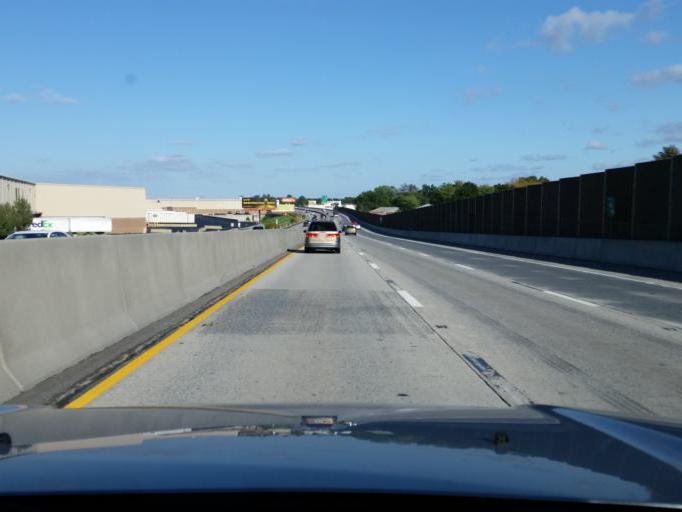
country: US
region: Pennsylvania
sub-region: Cumberland County
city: Lower Allen
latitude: 40.2352
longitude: -76.9076
